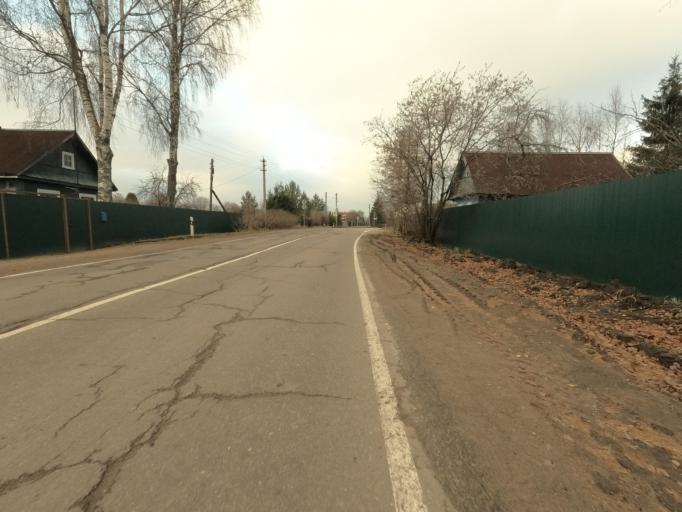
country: RU
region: Leningrad
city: Mga
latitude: 59.7739
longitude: 31.0240
